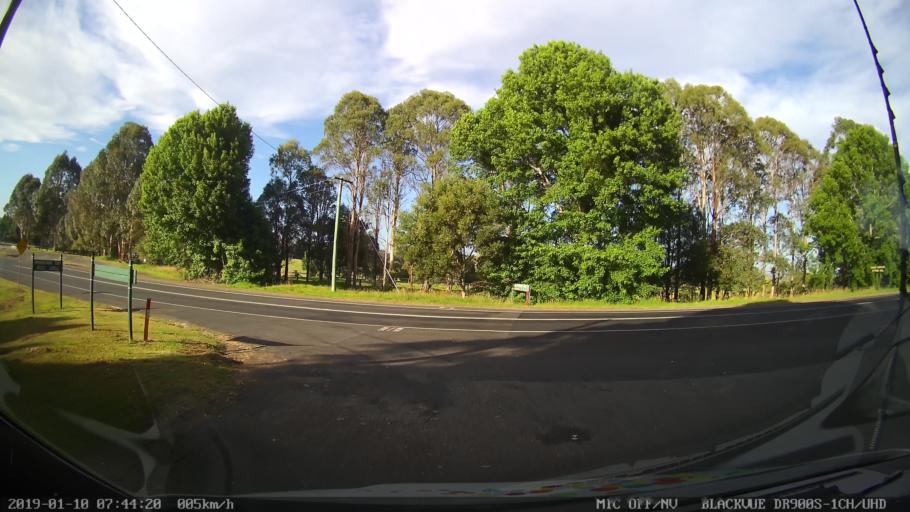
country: AU
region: New South Wales
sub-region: Bellingen
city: Dorrigo
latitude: -30.3741
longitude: 152.7251
